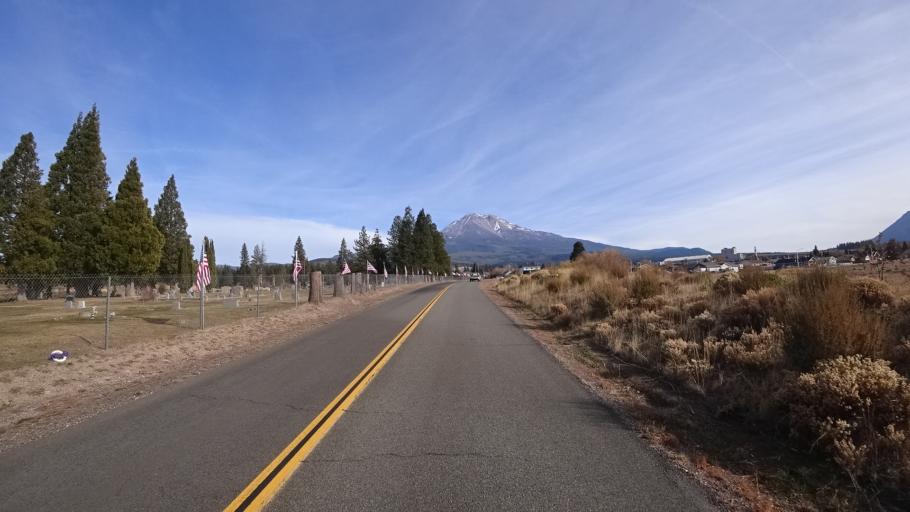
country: US
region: California
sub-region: Siskiyou County
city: Weed
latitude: 41.4398
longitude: -122.3837
